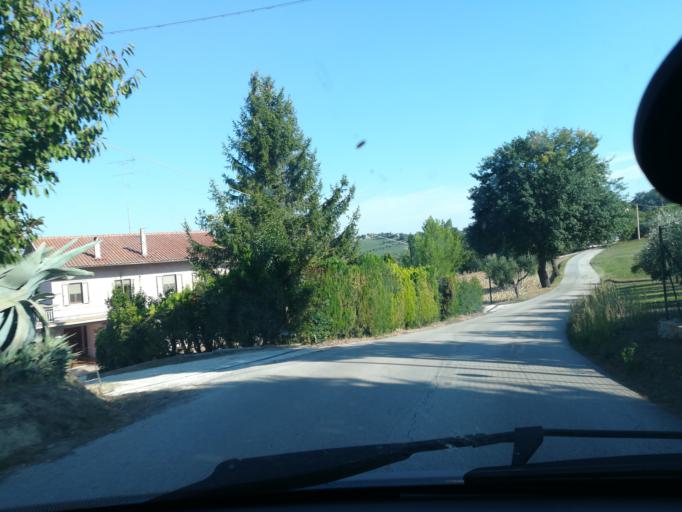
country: IT
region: The Marches
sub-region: Provincia di Macerata
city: Macerata
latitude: 43.3078
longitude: 13.4757
